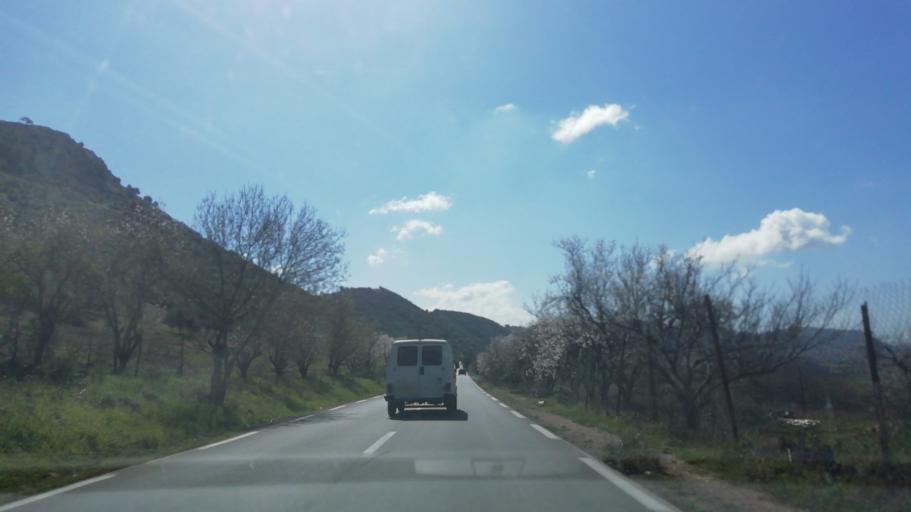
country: DZ
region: Mascara
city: Mascara
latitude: 35.4724
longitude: 0.1558
